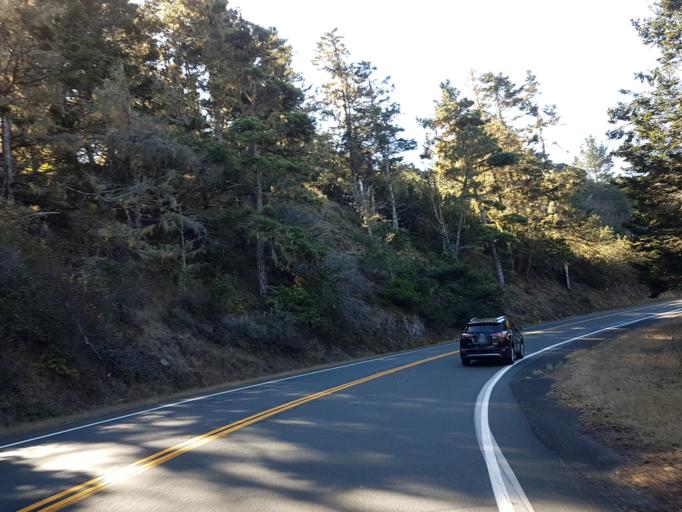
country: US
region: California
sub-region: Mendocino County
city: Boonville
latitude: 39.0207
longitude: -123.6851
